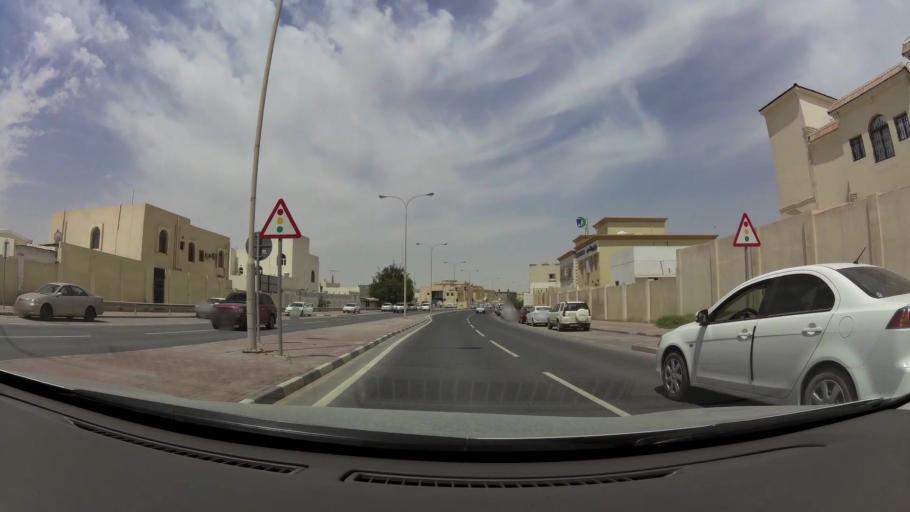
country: QA
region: Baladiyat ar Rayyan
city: Ar Rayyan
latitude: 25.2932
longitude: 51.4131
